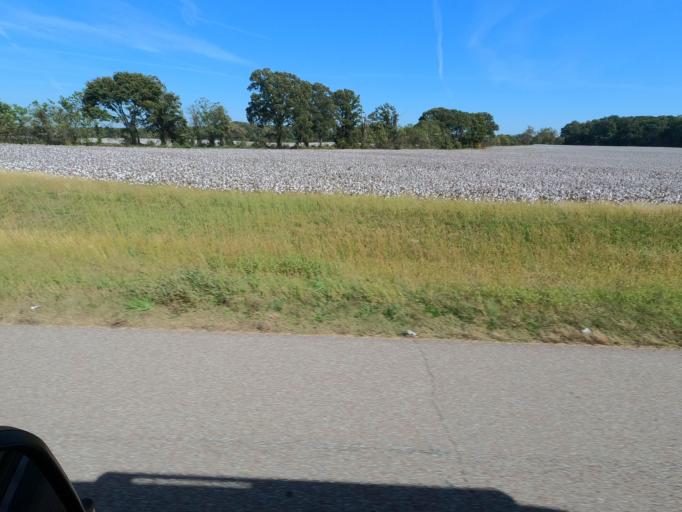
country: US
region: Tennessee
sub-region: Crockett County
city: Alamo
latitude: 35.8714
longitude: -89.2161
